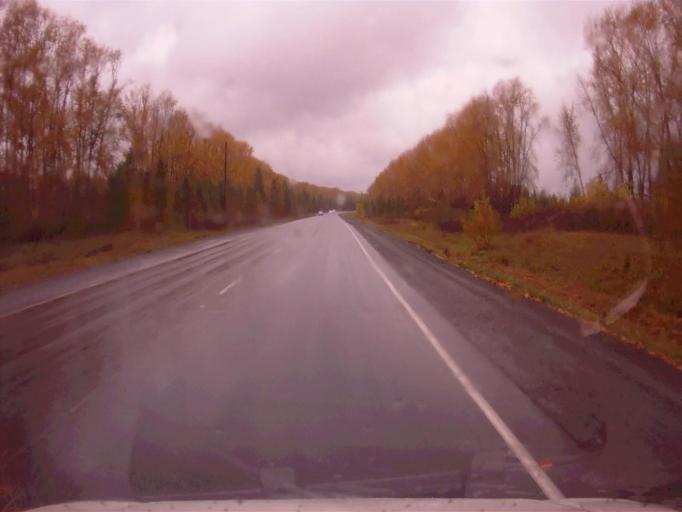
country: RU
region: Chelyabinsk
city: Argayash
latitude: 55.4488
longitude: 60.9423
